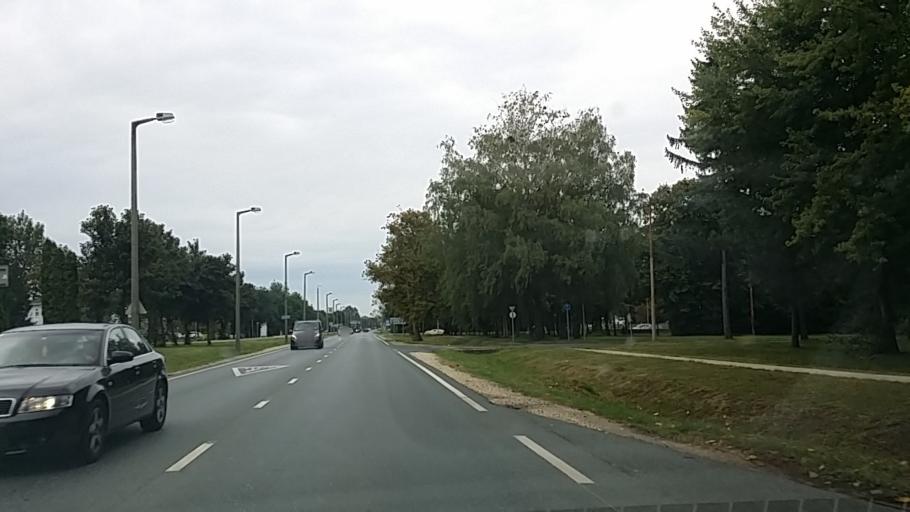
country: HU
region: Gyor-Moson-Sopron
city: Kapuvar
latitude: 47.5914
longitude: 17.0418
